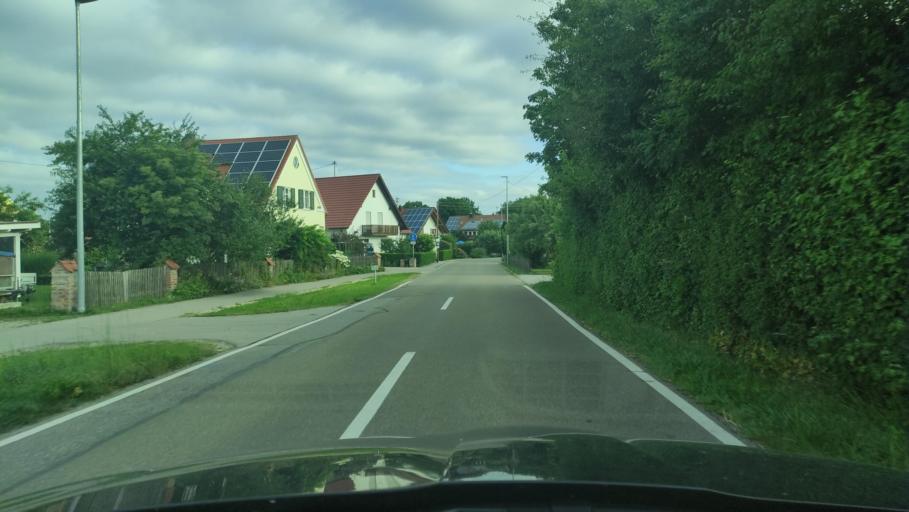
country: DE
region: Bavaria
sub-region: Swabia
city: Deisenhausen
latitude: 48.2863
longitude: 10.3072
